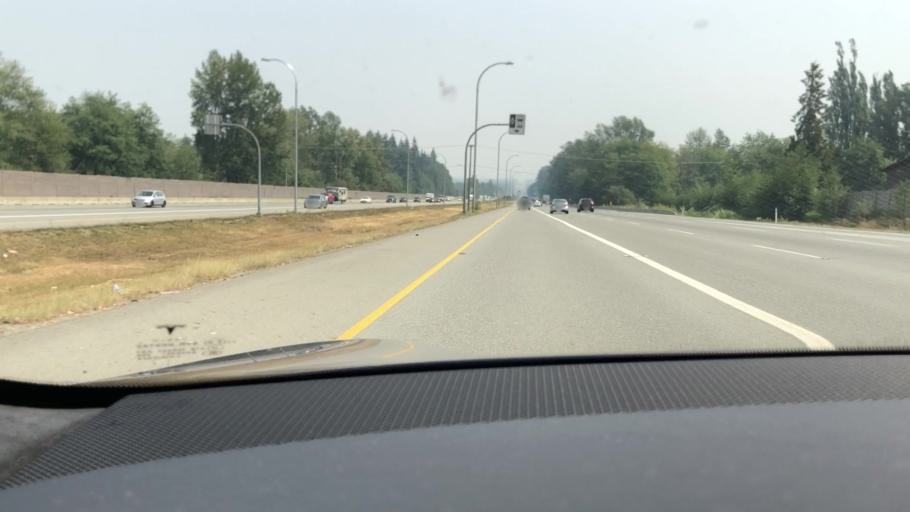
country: CA
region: British Columbia
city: Pitt Meadows
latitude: 49.1796
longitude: -122.7280
